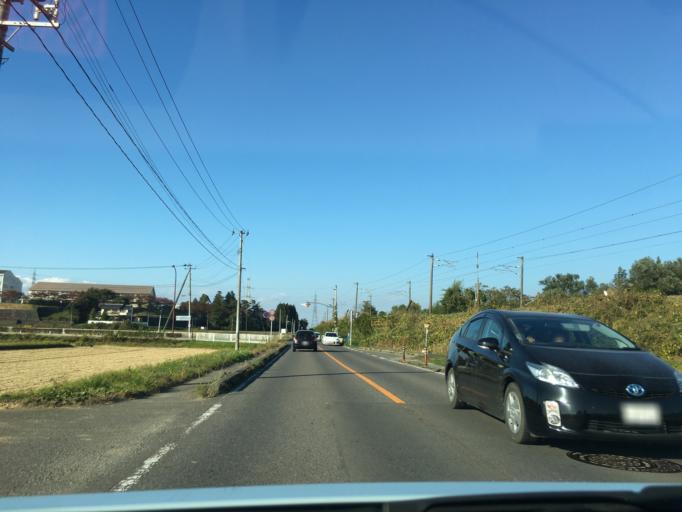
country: JP
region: Fukushima
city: Sukagawa
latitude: 37.3285
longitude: 140.3732
